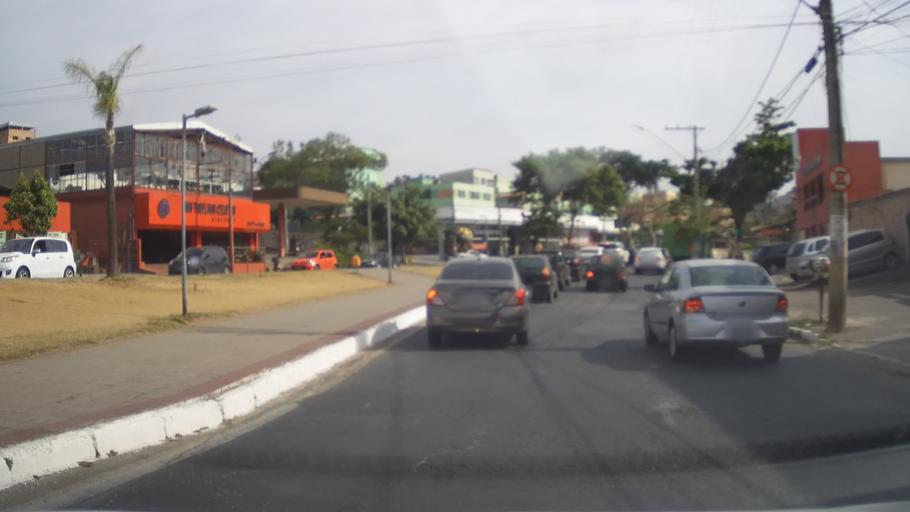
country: BR
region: Minas Gerais
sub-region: Contagem
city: Contagem
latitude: -19.9477
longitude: -44.0517
